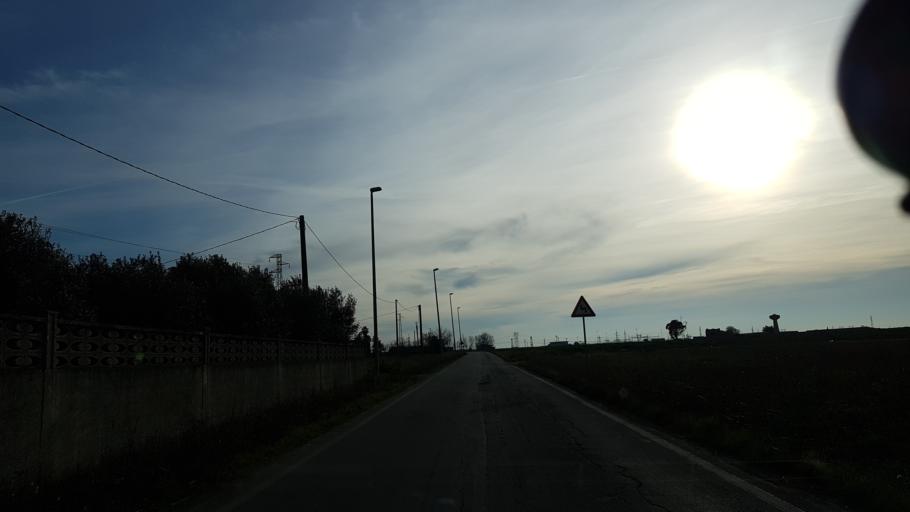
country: IT
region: Apulia
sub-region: Provincia di Brindisi
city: Brindisi
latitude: 40.6130
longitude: 17.9152
